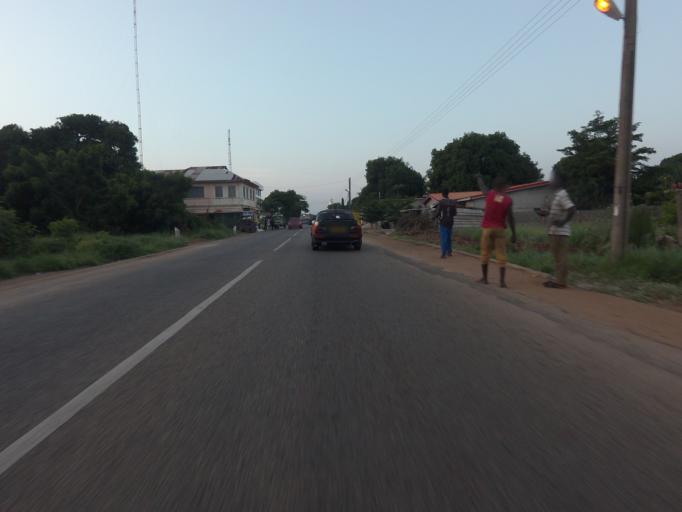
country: GH
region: Volta
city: Keta
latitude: 5.8796
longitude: 0.9818
